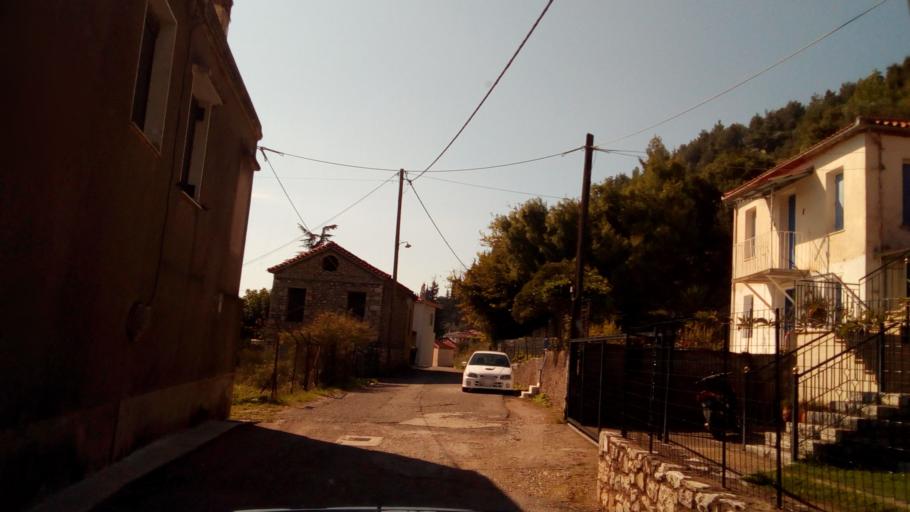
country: GR
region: West Greece
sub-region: Nomos Aitolias kai Akarnanias
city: Nafpaktos
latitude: 38.3990
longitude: 21.8428
